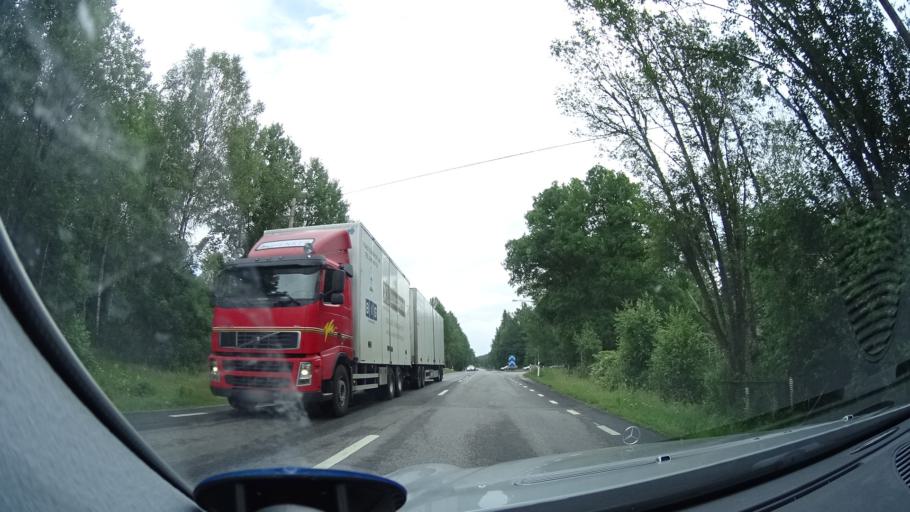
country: SE
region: Kronoberg
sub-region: Tingsryds Kommun
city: Tingsryd
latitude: 56.4692
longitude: 15.0098
